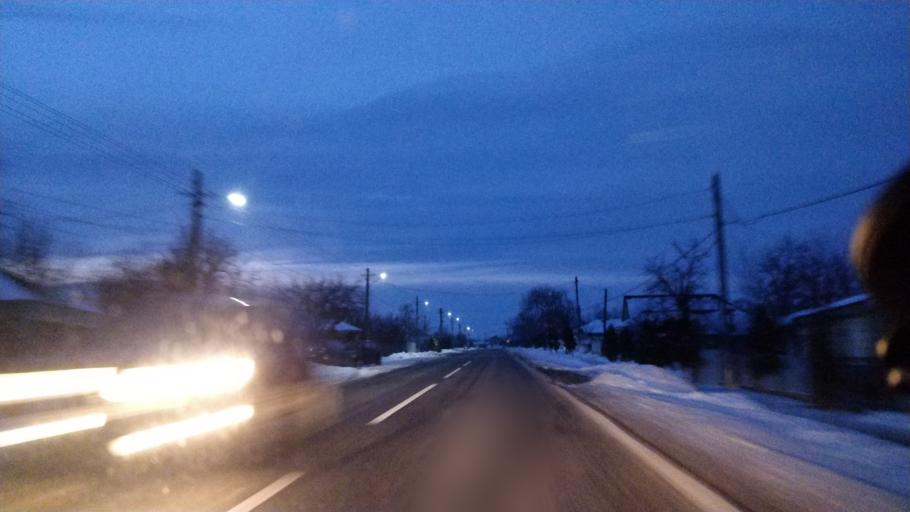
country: RO
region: Vrancea
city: Vulturu de Sus
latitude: 45.6328
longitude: 27.3848
